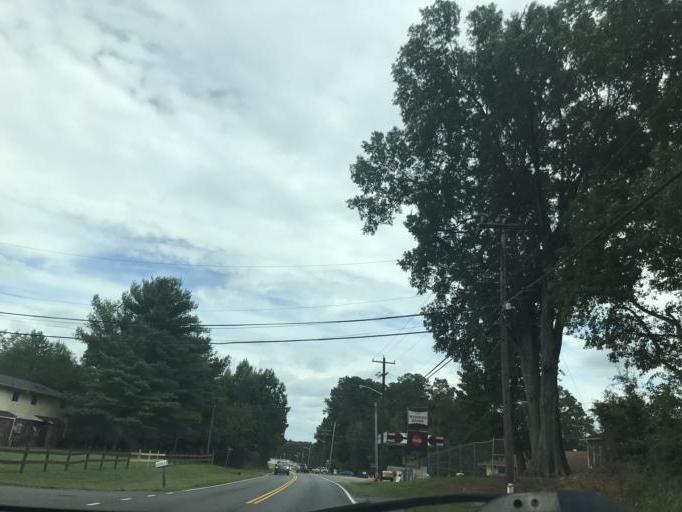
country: US
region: South Carolina
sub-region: Cherokee County
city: Gaffney
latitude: 35.0910
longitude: -81.6524
